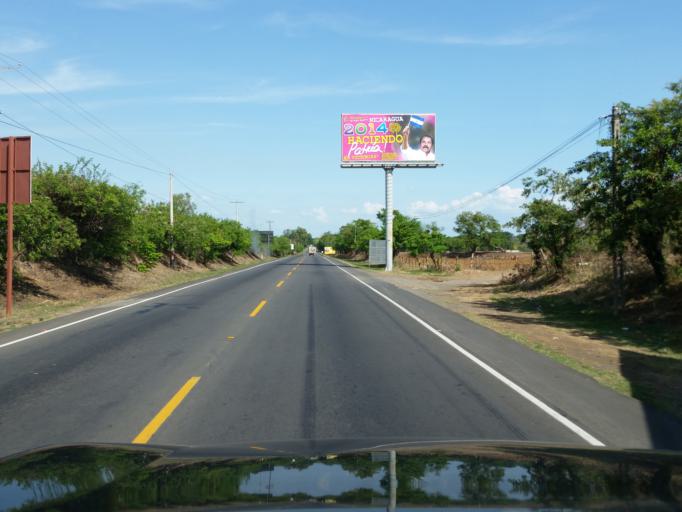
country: NI
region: Leon
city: Leon
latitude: 12.4086
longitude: -86.8612
